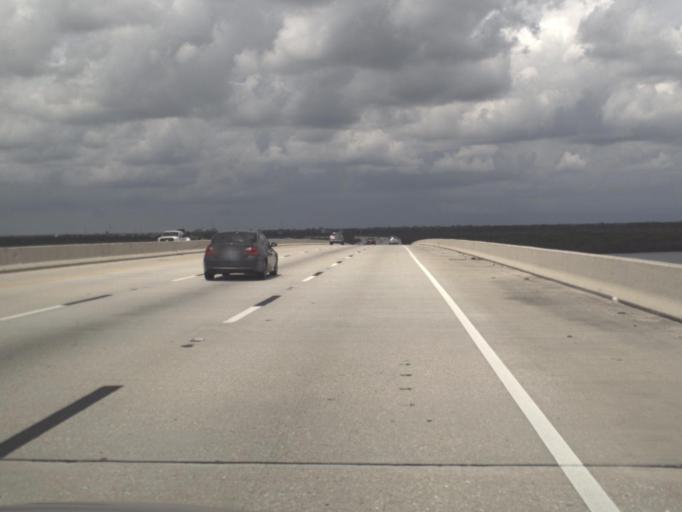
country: US
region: Florida
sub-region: Charlotte County
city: Harbour Heights
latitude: 26.9599
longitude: -82.0200
